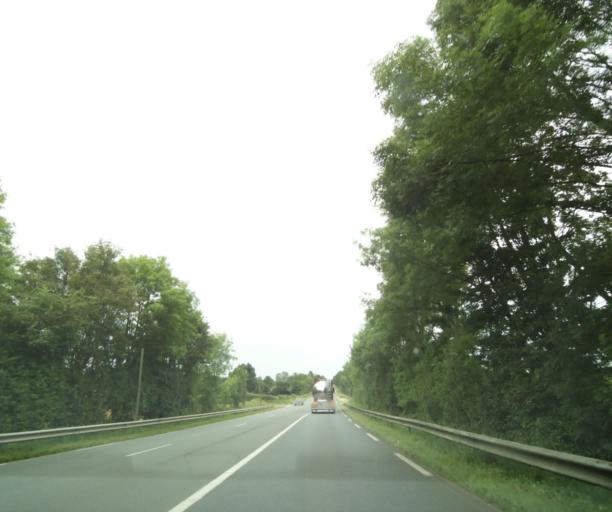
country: FR
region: Poitou-Charentes
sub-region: Departement des Deux-Sevres
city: Champdeniers-Saint-Denis
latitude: 46.4814
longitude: -0.3586
